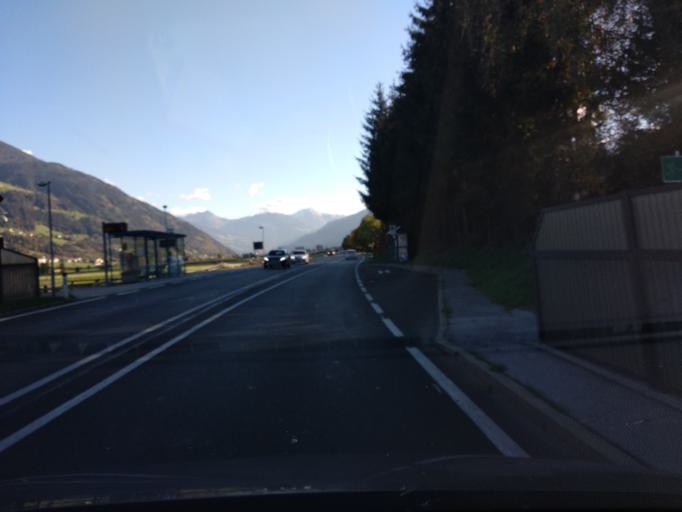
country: AT
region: Tyrol
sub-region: Politischer Bezirk Schwaz
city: Fugenberg
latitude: 47.3632
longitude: 11.8516
